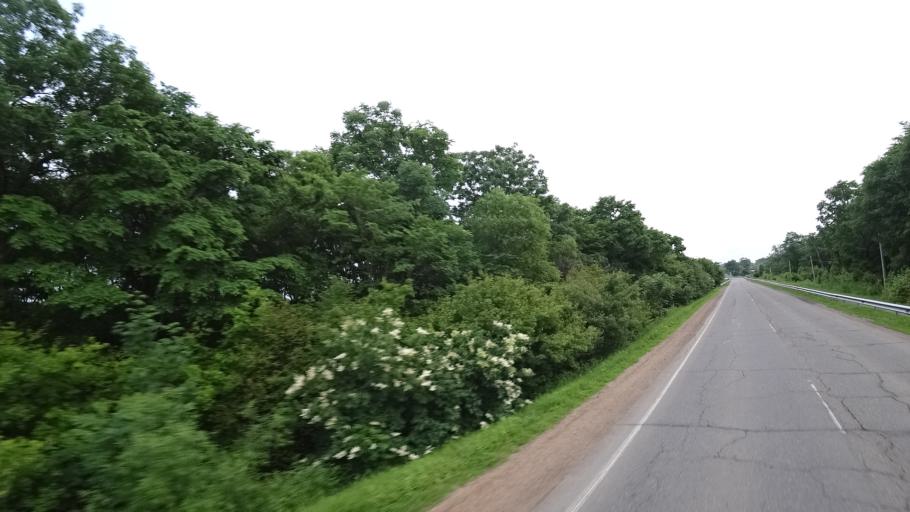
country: RU
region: Primorskiy
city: Novosysoyevka
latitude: 44.2331
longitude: 133.3774
